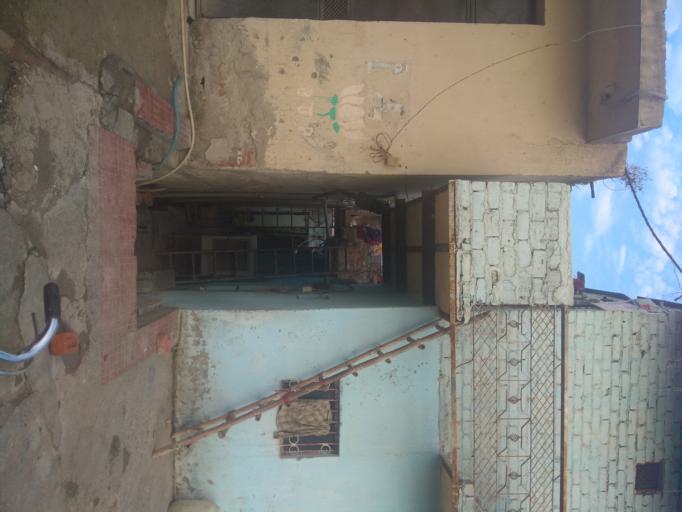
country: IN
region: NCT
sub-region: West Delhi
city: Nangloi Jat
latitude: 28.6378
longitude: 77.0611
